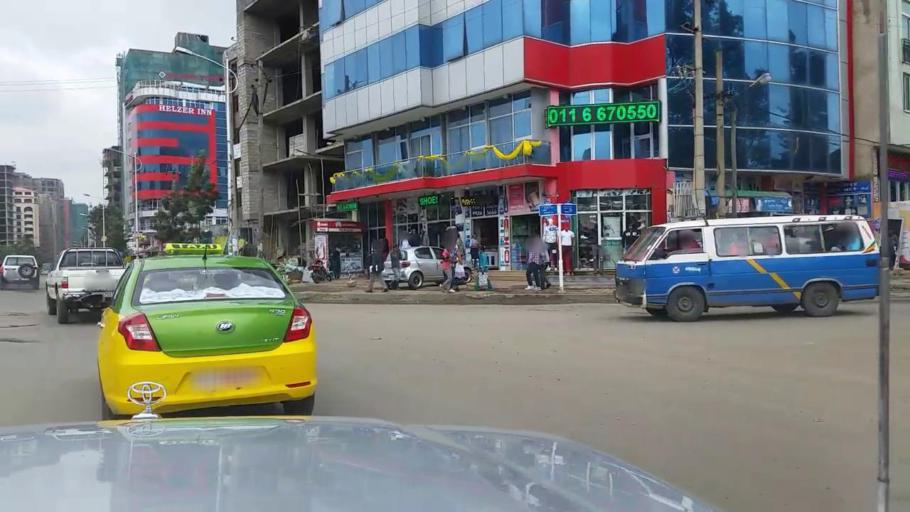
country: ET
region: Adis Abeba
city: Addis Ababa
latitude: 8.9980
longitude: 38.7869
